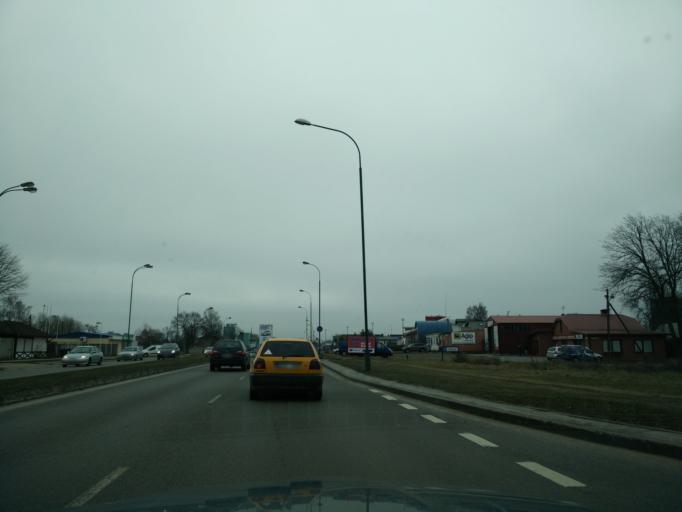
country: LT
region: Klaipedos apskritis
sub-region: Klaipeda
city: Klaipeda
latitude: 55.6918
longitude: 21.1429
